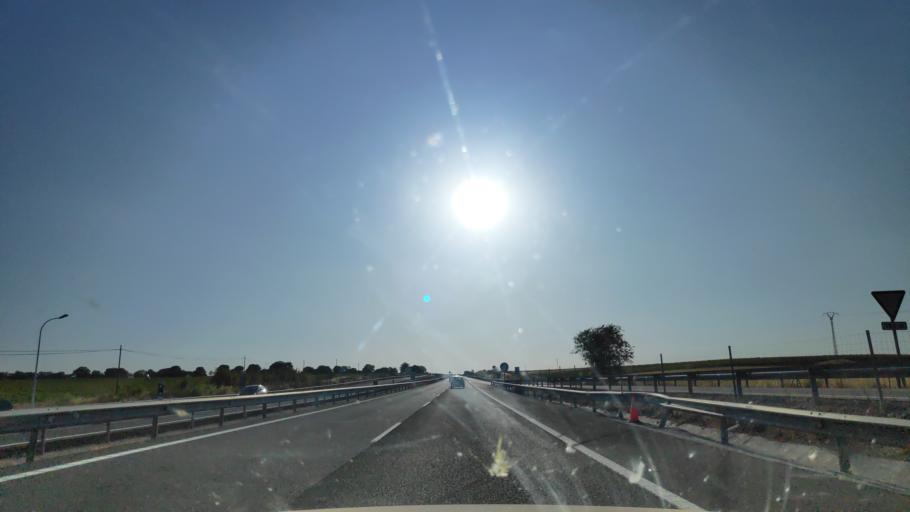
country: ES
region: Castille-La Mancha
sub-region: Provincia de Cuenca
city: Saelices
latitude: 39.9133
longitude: -2.7468
